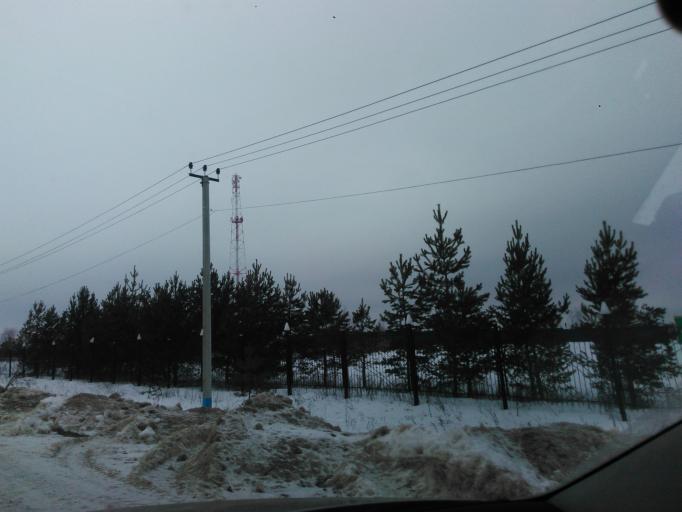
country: RU
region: Moskovskaya
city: Podosinki
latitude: 56.2757
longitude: 37.5986
